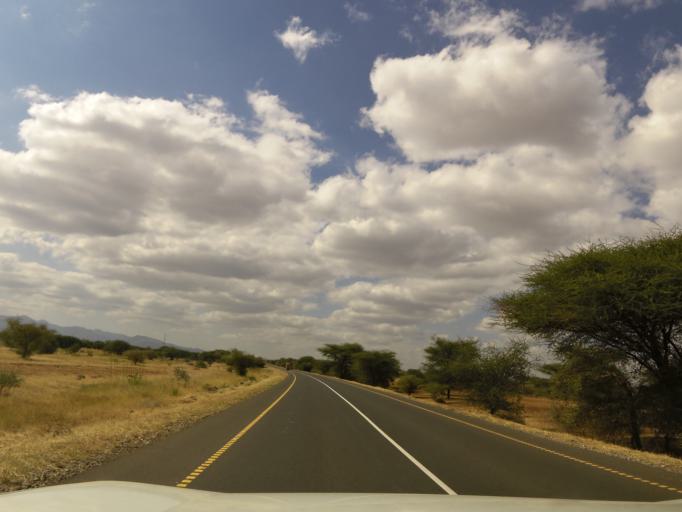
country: TZ
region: Arusha
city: Mto wa Mbu
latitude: -3.5772
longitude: 36.0734
